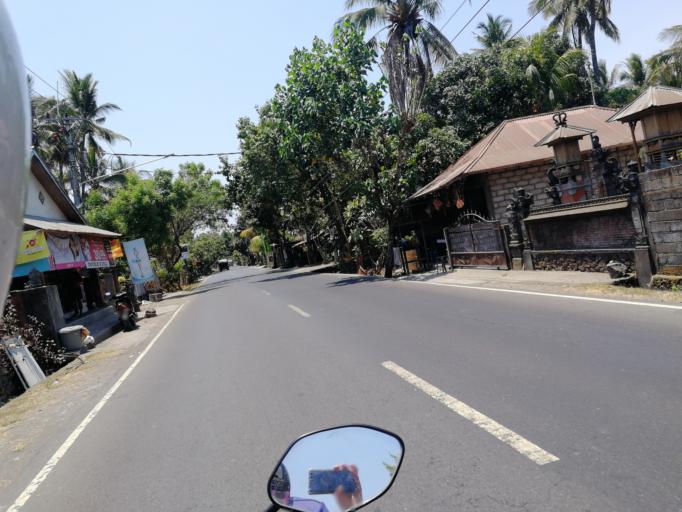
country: ID
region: Bali
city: Banjar Trunyan
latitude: -8.1502
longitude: 115.4101
